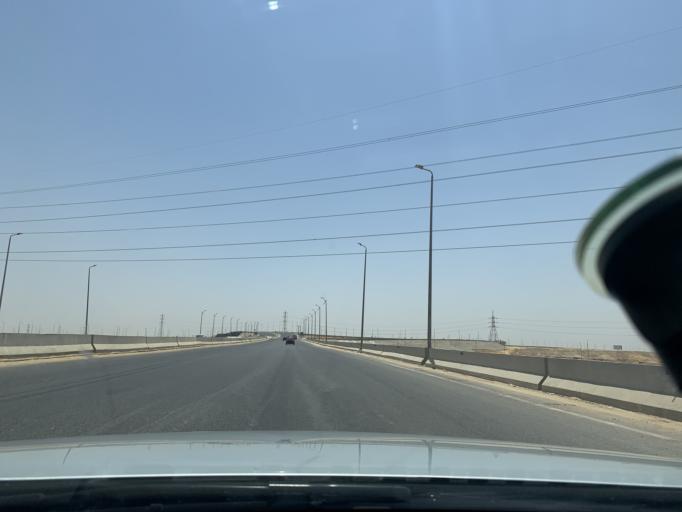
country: EG
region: Muhafazat al Qahirah
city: Halwan
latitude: 29.9730
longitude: 31.4699
